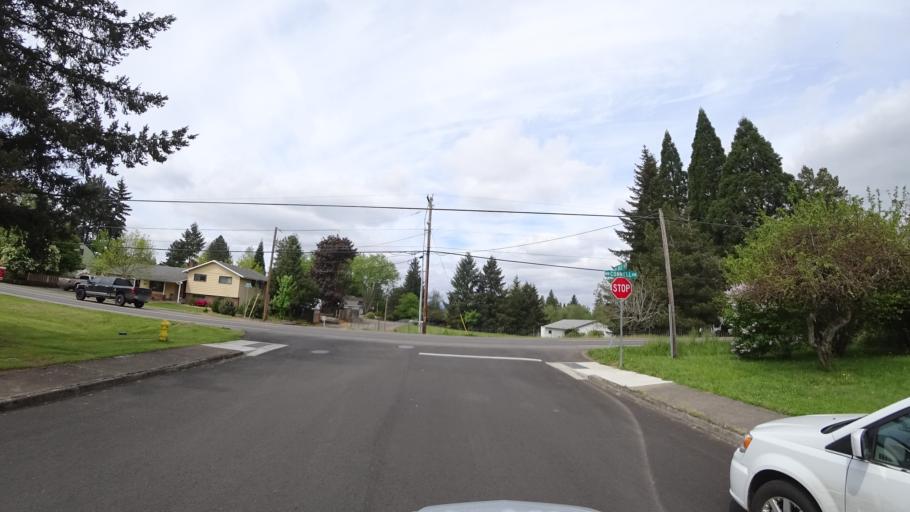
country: US
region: Oregon
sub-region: Washington County
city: Hillsboro
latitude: 45.5330
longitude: -122.9928
